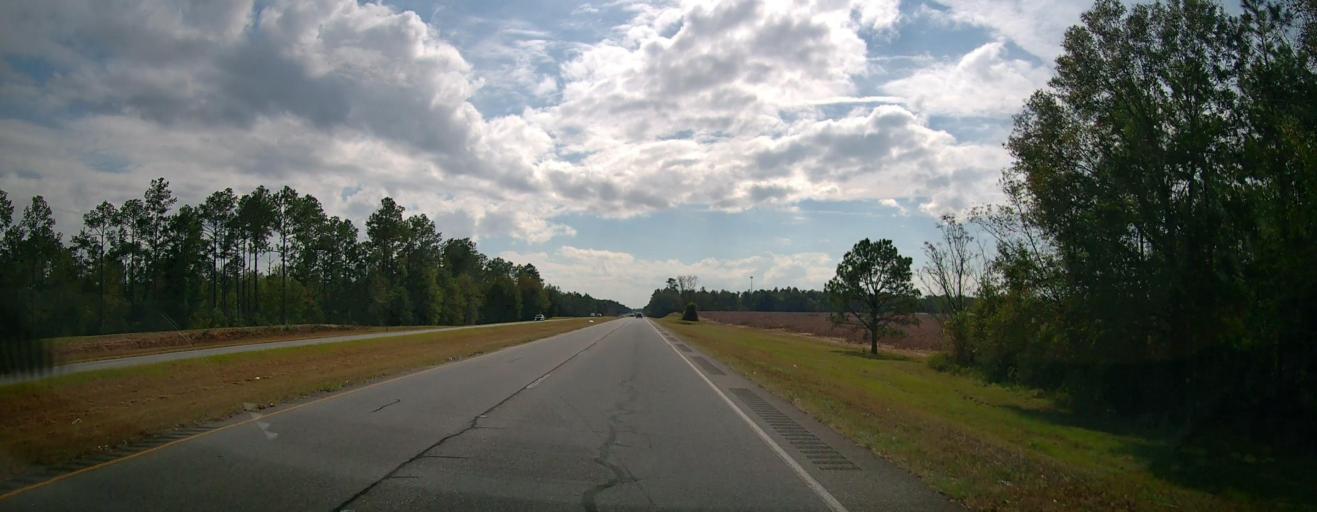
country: US
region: Georgia
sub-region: Mitchell County
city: Camilla
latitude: 31.3155
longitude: -84.1751
